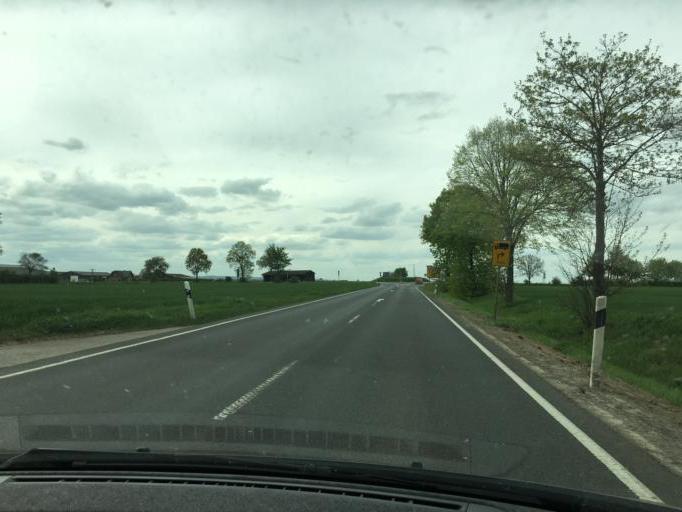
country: DE
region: North Rhine-Westphalia
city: Zulpich
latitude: 50.7315
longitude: 6.6660
